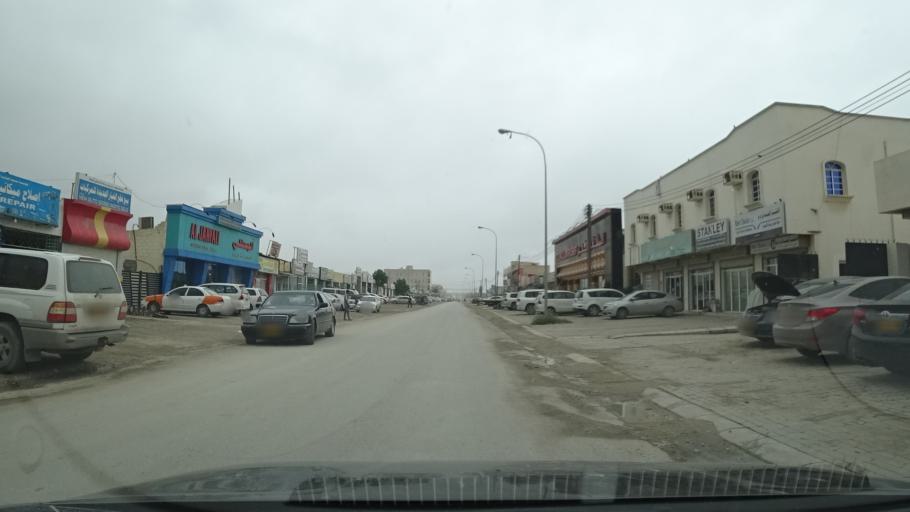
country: OM
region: Zufar
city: Salalah
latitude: 17.0157
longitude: 54.0472
